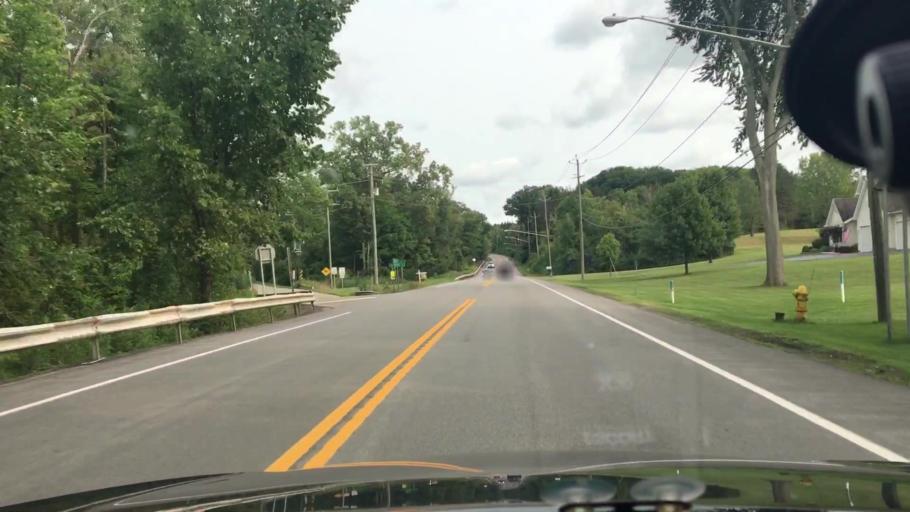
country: US
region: New York
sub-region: Erie County
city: Orchard Park
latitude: 42.7391
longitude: -78.7365
